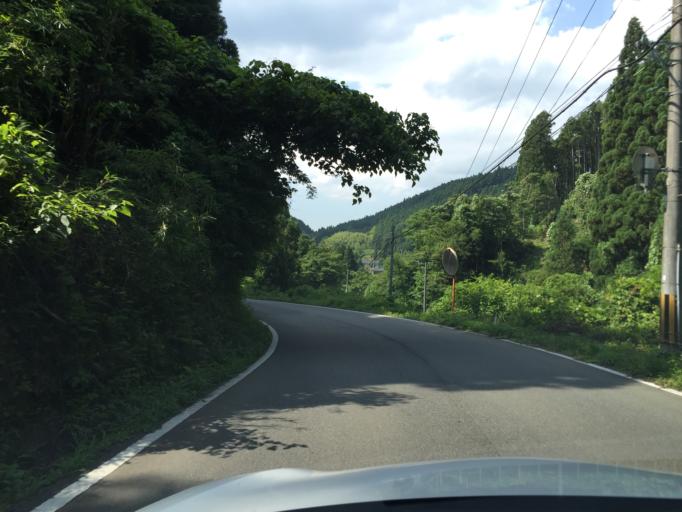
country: JP
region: Fukushima
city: Iwaki
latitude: 36.9987
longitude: 140.7107
